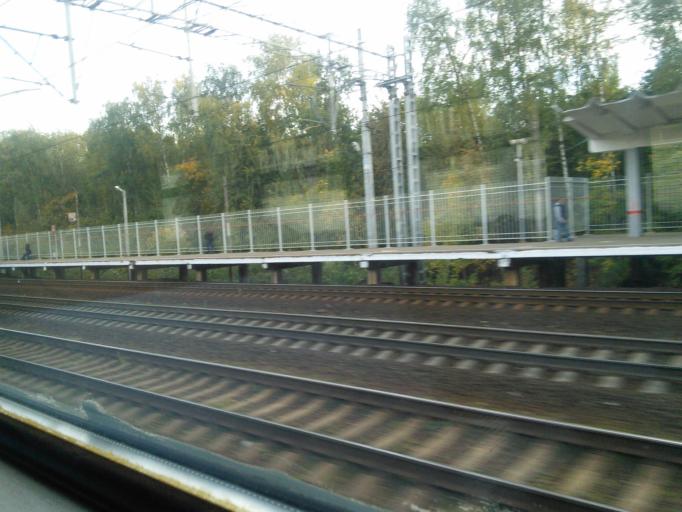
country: RU
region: Moskovskaya
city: Levoberezhnaya
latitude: 55.8869
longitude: 37.4690
